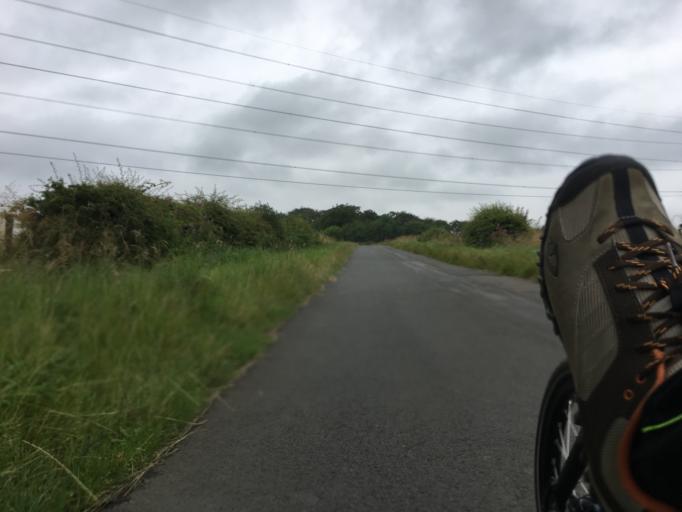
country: GB
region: Scotland
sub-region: West Lothian
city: Mid Calder
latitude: 55.8509
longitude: -3.5110
